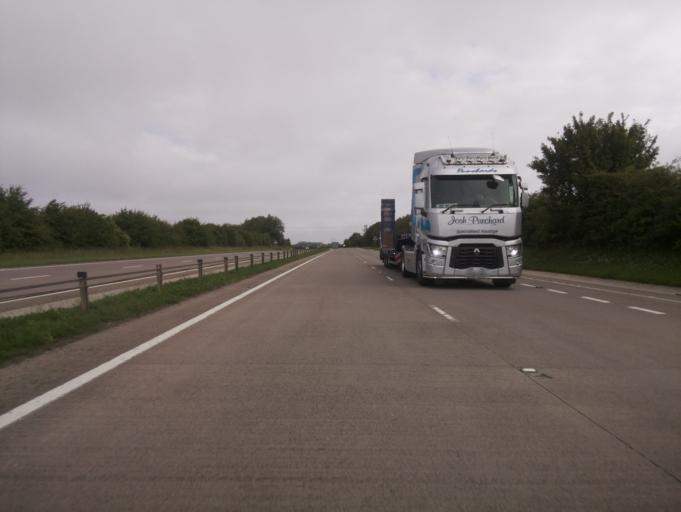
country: GB
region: England
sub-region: Gloucestershire
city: Cirencester
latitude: 51.7359
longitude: -1.9565
